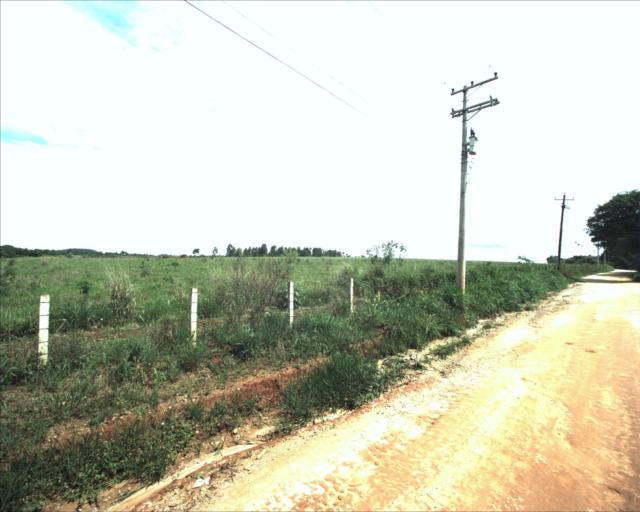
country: BR
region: Sao Paulo
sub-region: Aracoiaba Da Serra
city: Aracoiaba da Serra
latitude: -23.5533
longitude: -47.5476
